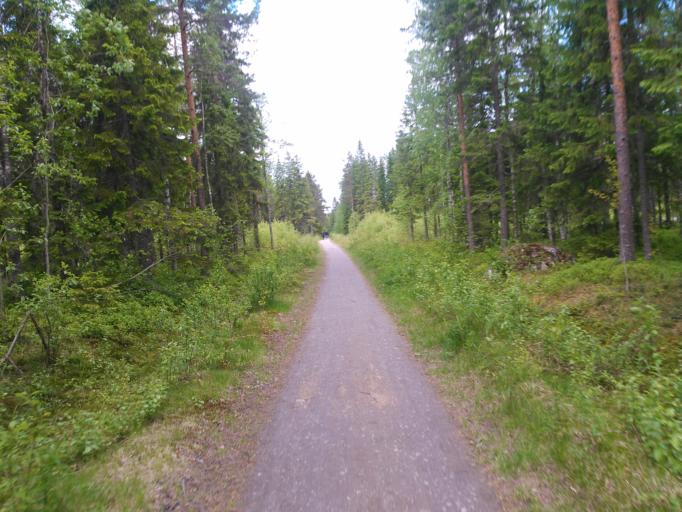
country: SE
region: Vaesterbotten
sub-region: Umea Kommun
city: Ersmark
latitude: 63.8656
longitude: 20.3337
